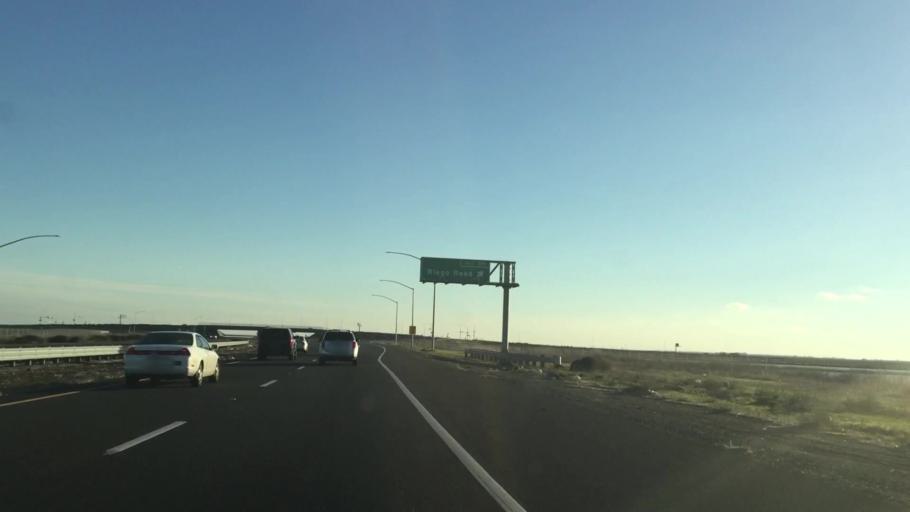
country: US
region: California
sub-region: Sacramento County
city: Elverta
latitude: 38.7569
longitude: -121.5433
